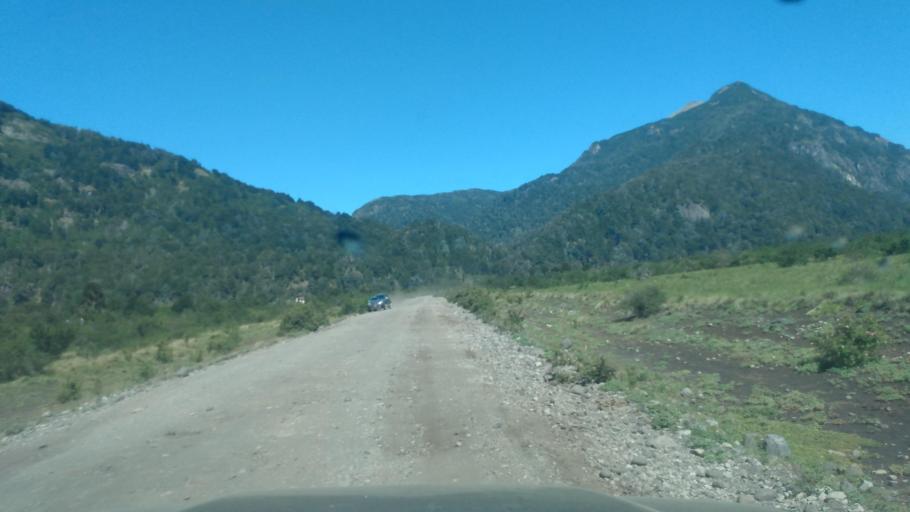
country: AR
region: Neuquen
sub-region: Departamento de Lacar
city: San Martin de los Andes
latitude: -39.7459
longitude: -71.5163
